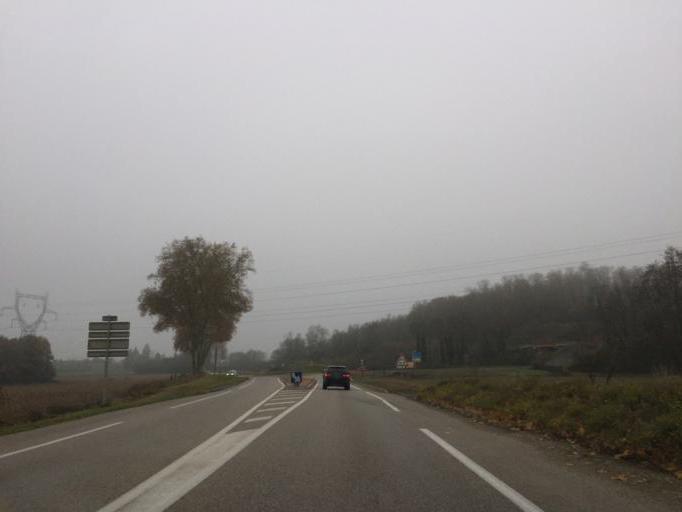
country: FR
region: Rhone-Alpes
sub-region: Departement de l'Ain
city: Mionnay
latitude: 45.8819
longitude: 4.9103
